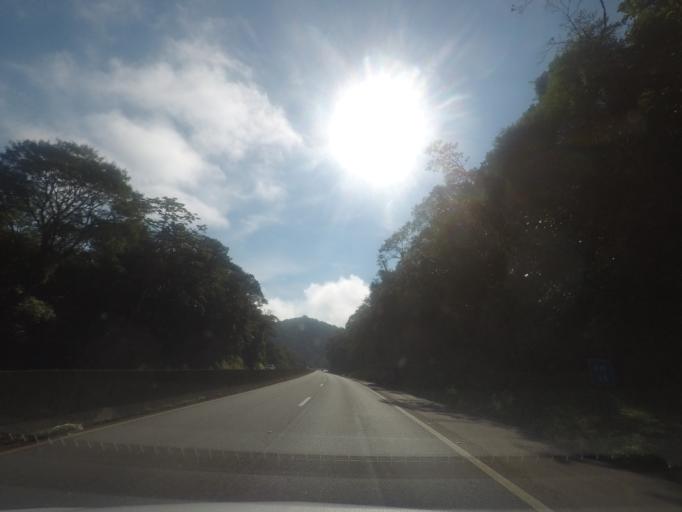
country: BR
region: Parana
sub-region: Piraquara
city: Piraquara
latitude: -25.5949
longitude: -48.8975
